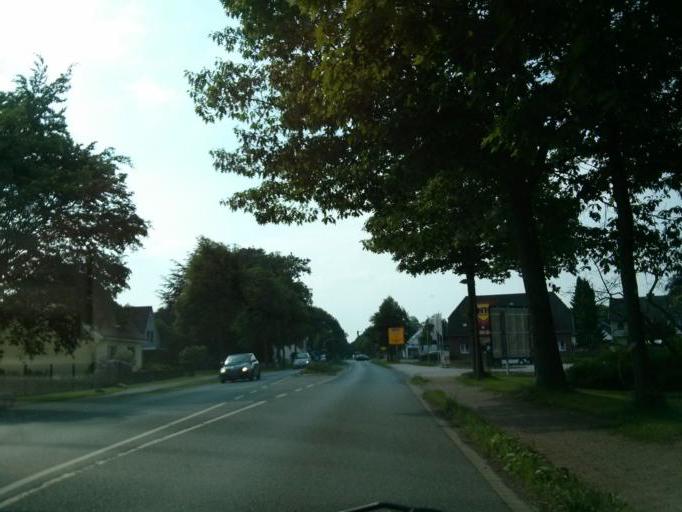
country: DE
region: Lower Saxony
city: Loxstedt
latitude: 53.4828
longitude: 8.6852
